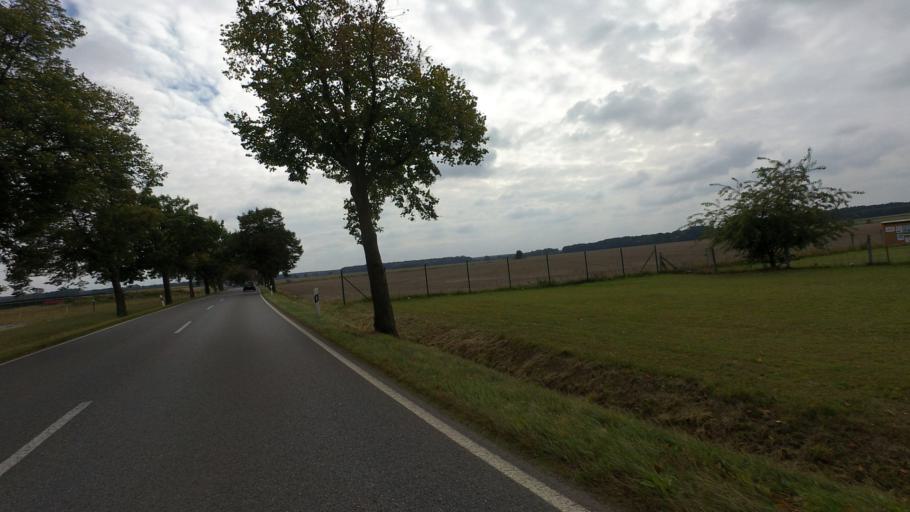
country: DE
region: Brandenburg
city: Golssen
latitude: 51.9469
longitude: 13.6474
